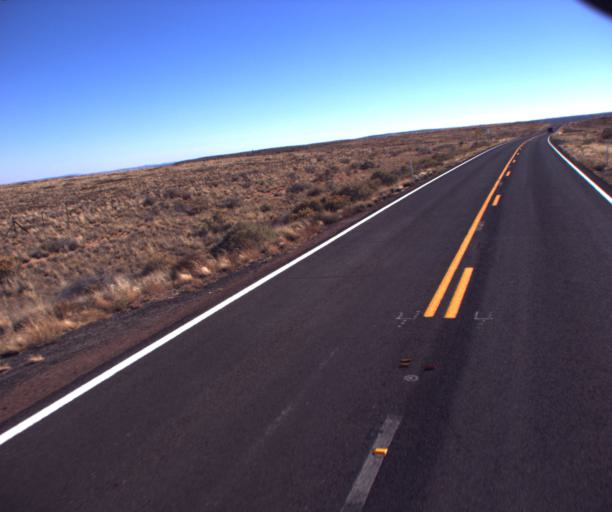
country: US
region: Arizona
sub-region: Coconino County
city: Tuba City
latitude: 35.9607
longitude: -110.9388
